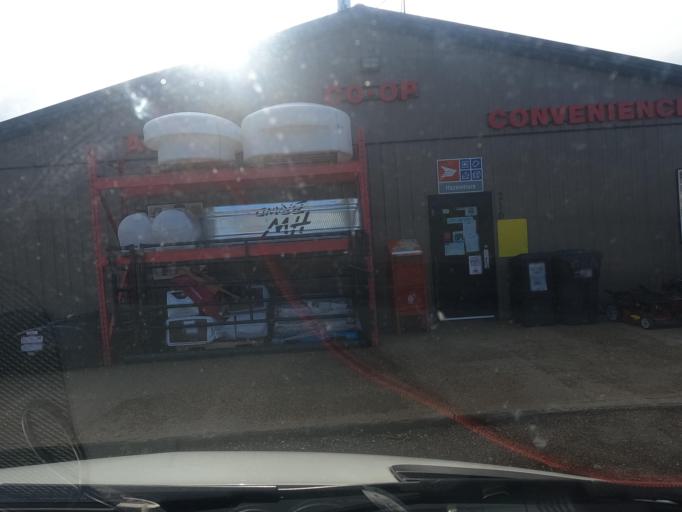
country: CA
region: Saskatchewan
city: Gravelbourg
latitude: 49.6868
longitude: -107.1376
